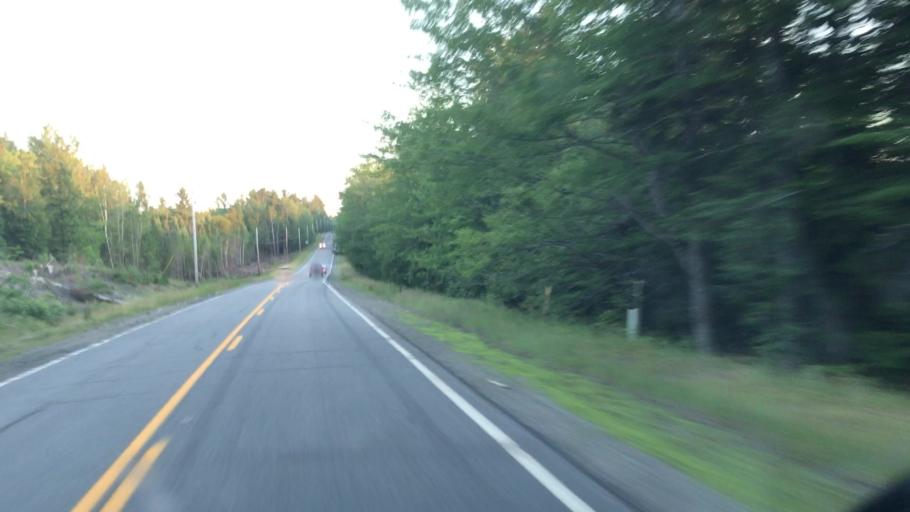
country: US
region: Maine
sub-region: Penobscot County
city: Medway
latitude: 45.5913
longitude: -68.3128
